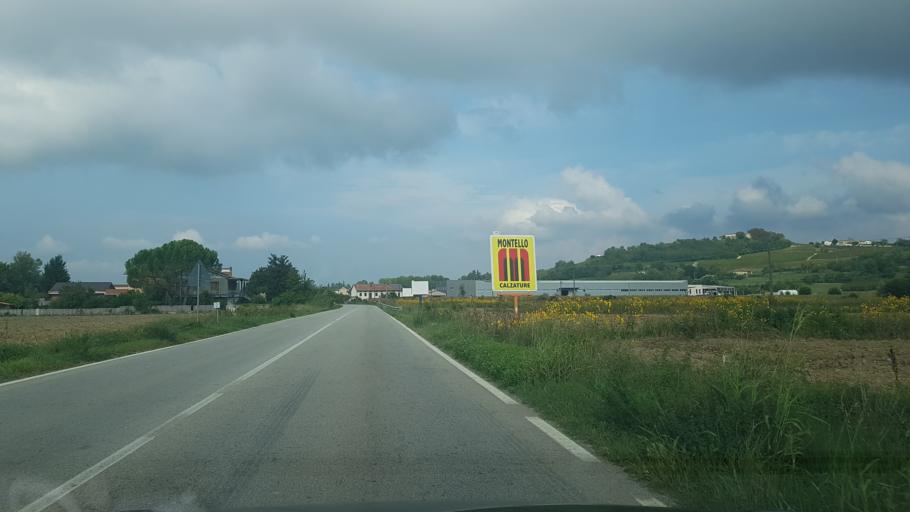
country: IT
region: Piedmont
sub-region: Provincia di Asti
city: Calamandrana
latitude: 44.7555
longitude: 8.3473
